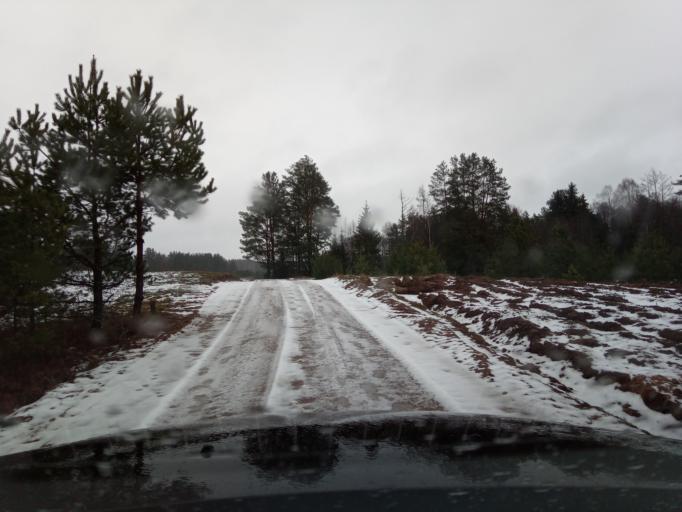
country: LT
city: Svencioneliai
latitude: 55.3365
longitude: 25.8064
